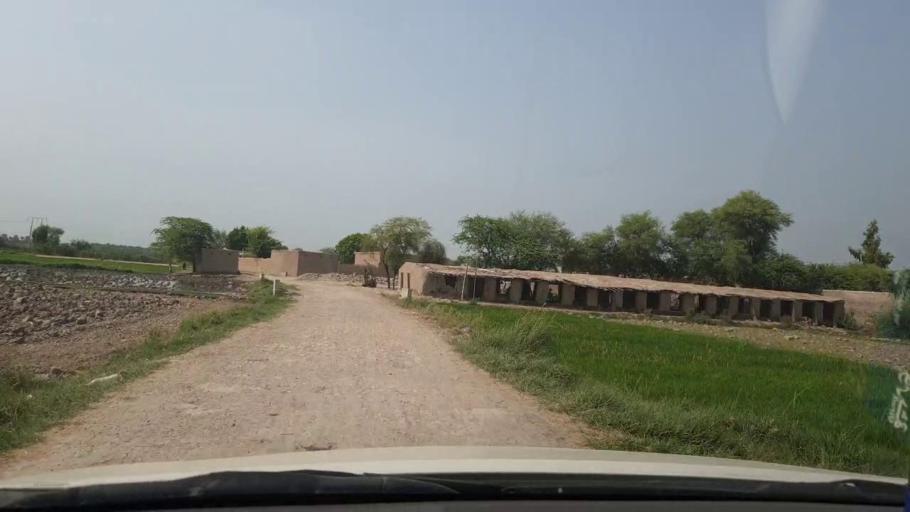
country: PK
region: Sindh
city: Shikarpur
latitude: 27.9811
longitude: 68.6738
